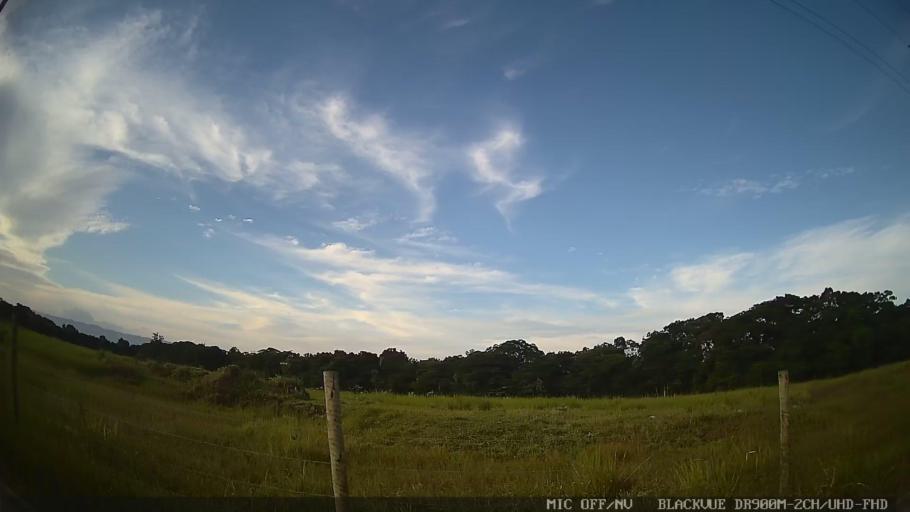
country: BR
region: Sao Paulo
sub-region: Itanhaem
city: Itanhaem
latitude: -24.1529
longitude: -46.7900
